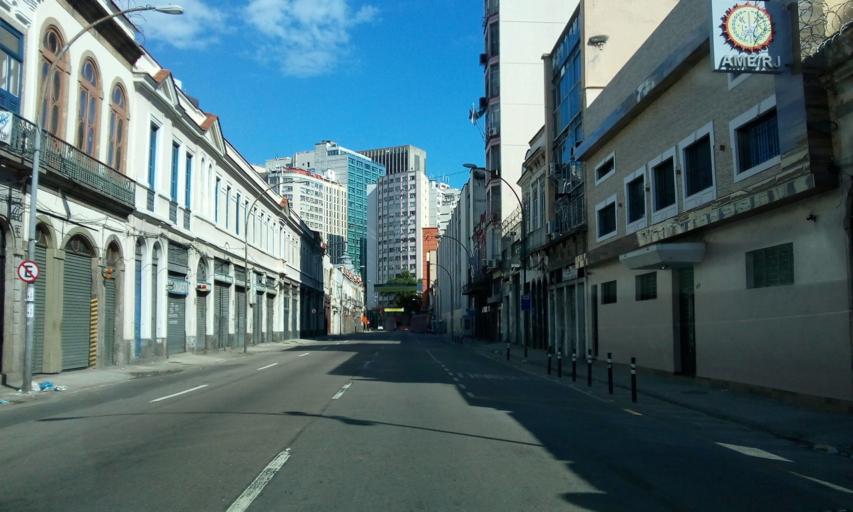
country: BR
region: Rio de Janeiro
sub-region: Rio De Janeiro
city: Rio de Janeiro
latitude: -22.9005
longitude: -43.1866
